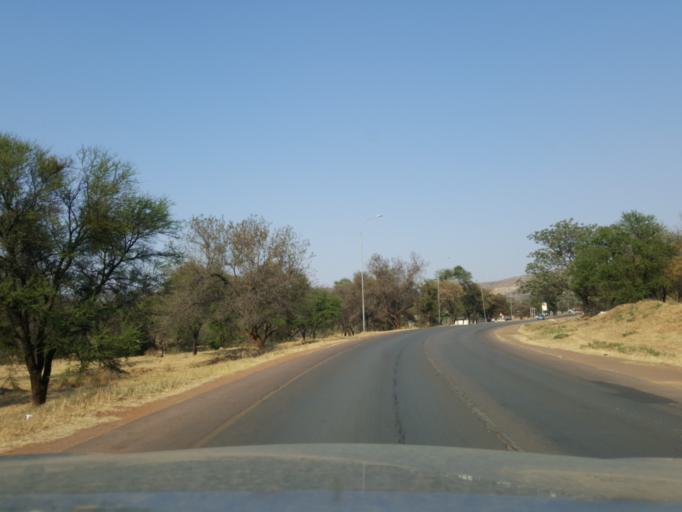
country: BW
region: South East
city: Lobatse
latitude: -25.2267
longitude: 25.6763
